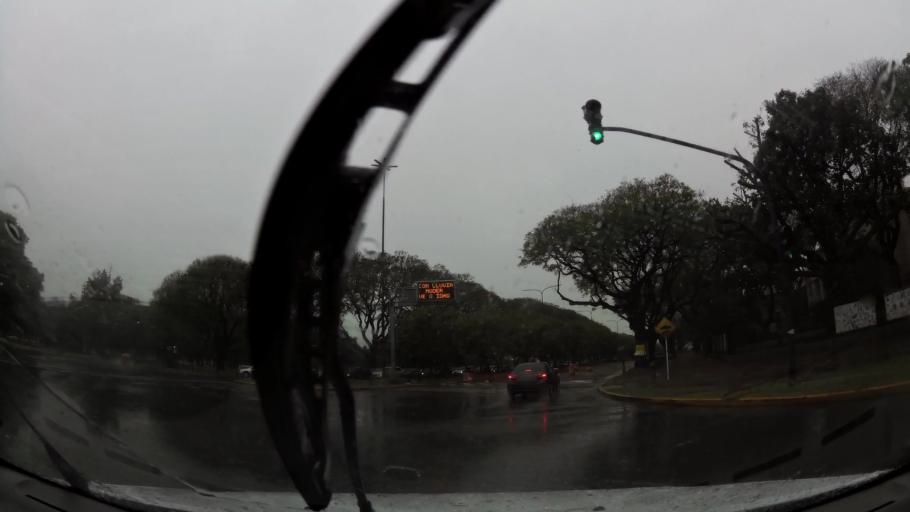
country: AR
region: Buenos Aires F.D.
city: Colegiales
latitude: -34.5652
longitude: -58.4198
